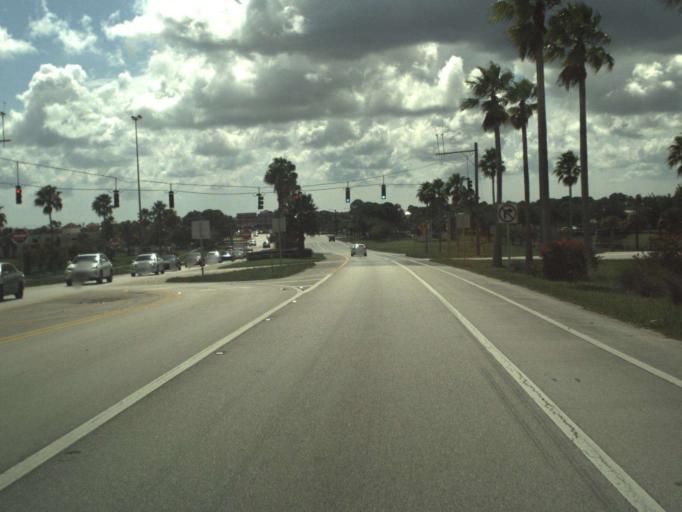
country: US
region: Florida
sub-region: Saint Lucie County
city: Port Saint Lucie
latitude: 27.3114
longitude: -80.4120
